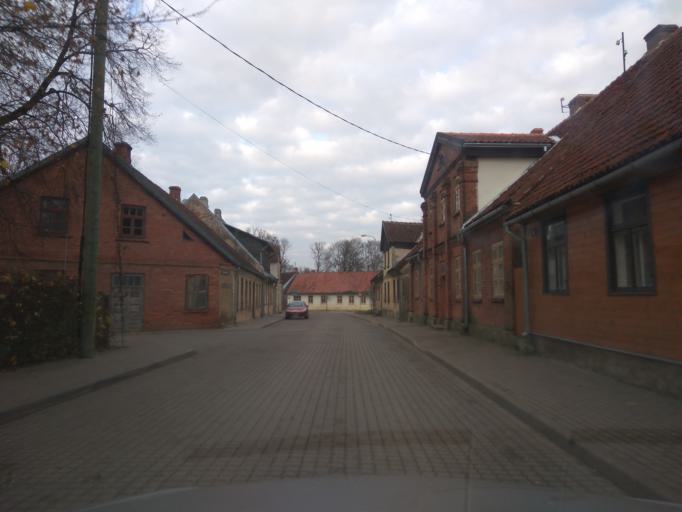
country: LV
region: Kuldigas Rajons
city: Kuldiga
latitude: 56.9643
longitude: 21.9721
